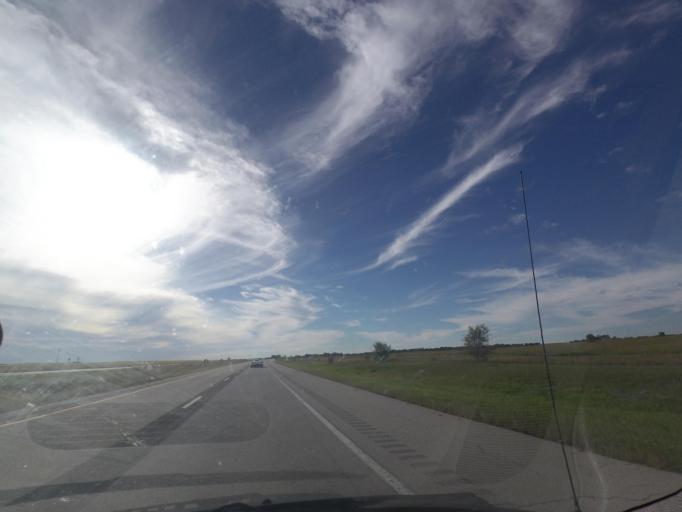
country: US
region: Illinois
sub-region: Sangamon County
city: Riverton
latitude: 39.8385
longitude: -89.3875
